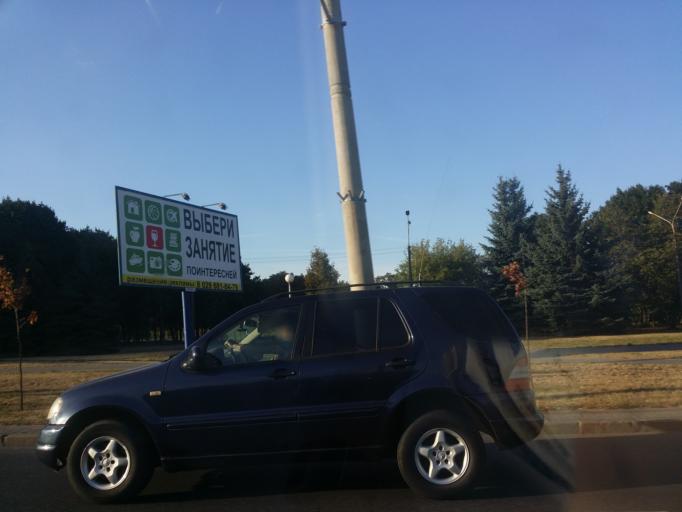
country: BY
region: Minsk
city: Minsk
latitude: 53.8780
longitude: 27.6134
